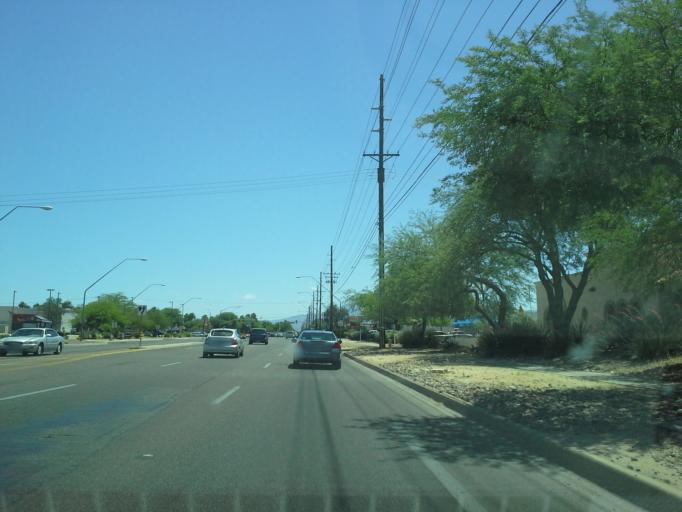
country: US
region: Arizona
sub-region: Pima County
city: Tucson
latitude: 32.2506
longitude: -110.8953
